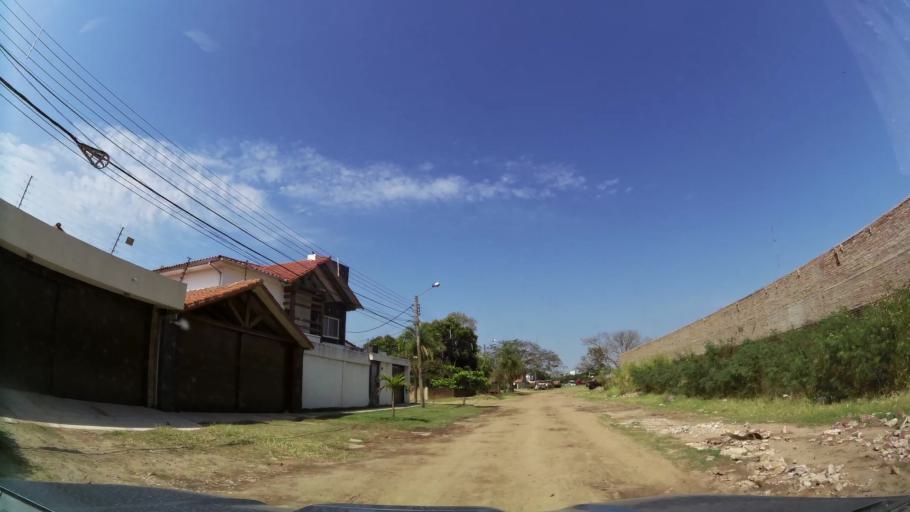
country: BO
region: Santa Cruz
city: Santa Cruz de la Sierra
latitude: -17.7499
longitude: -63.1599
